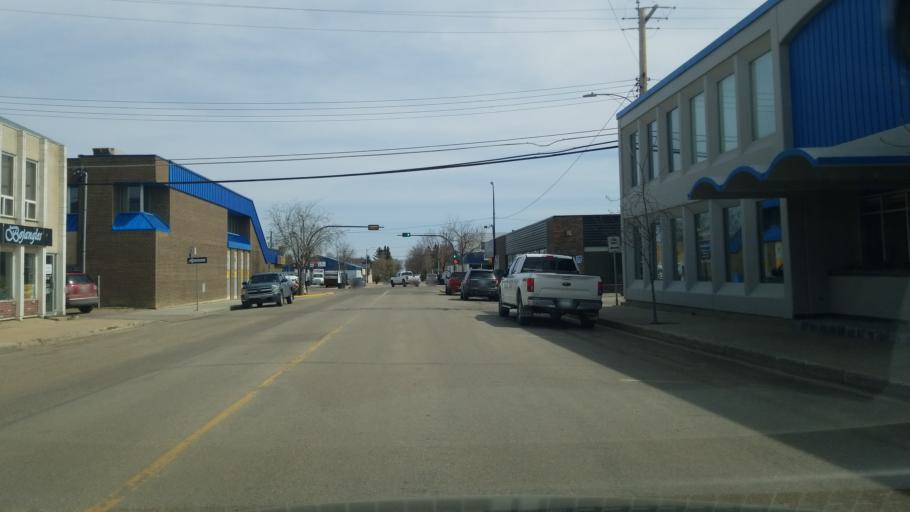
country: CA
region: Saskatchewan
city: Lloydminster
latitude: 53.2816
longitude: -110.0067
